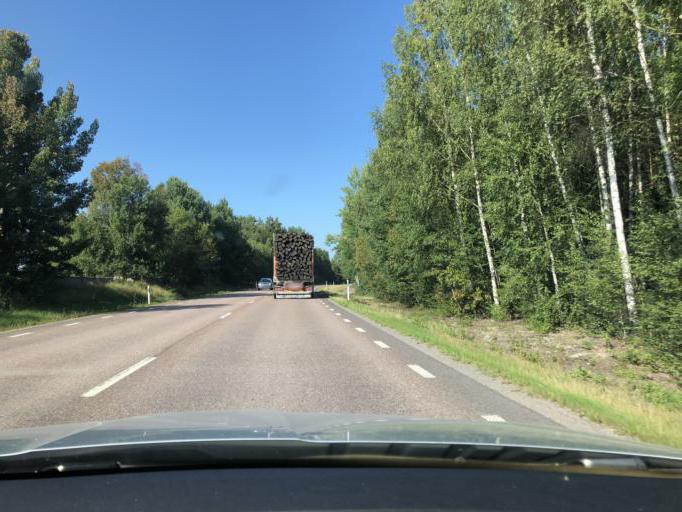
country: SE
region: Dalarna
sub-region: Faluns Kommun
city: Falun
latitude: 60.5756
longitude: 15.7722
